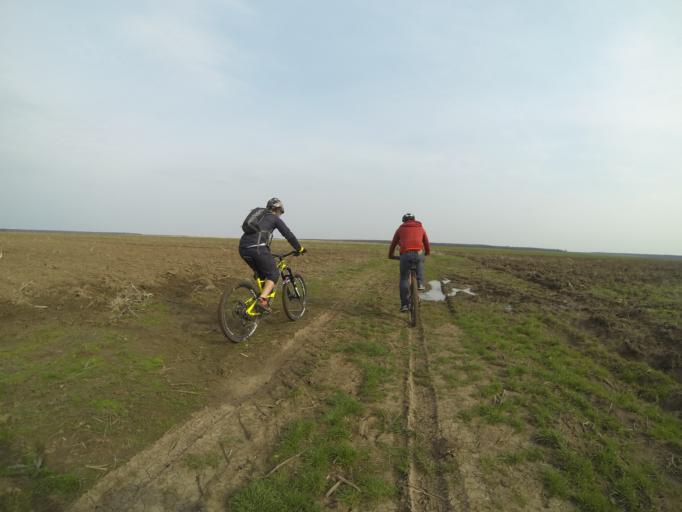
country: RO
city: Varvoru
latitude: 44.2639
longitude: 23.6722
